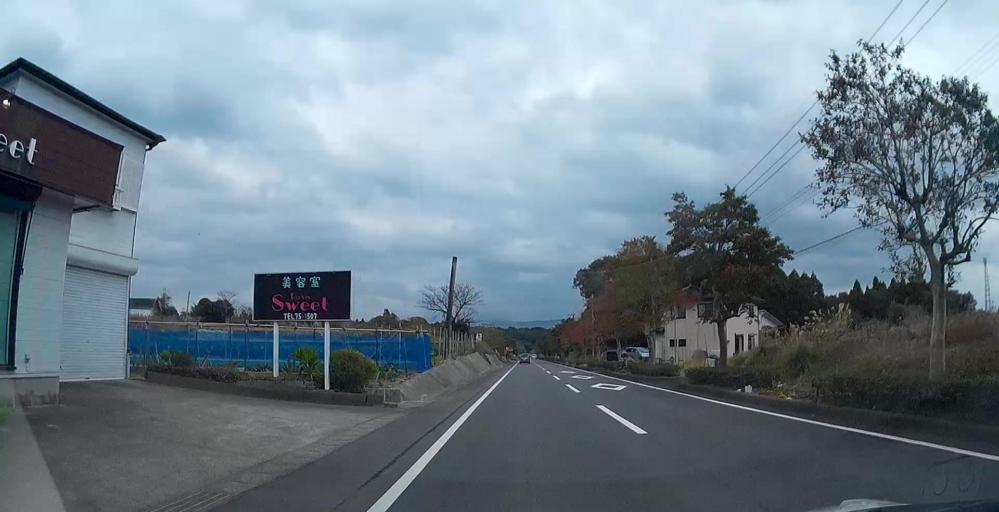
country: JP
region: Kagoshima
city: Akune
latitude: 32.0740
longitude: 130.2129
